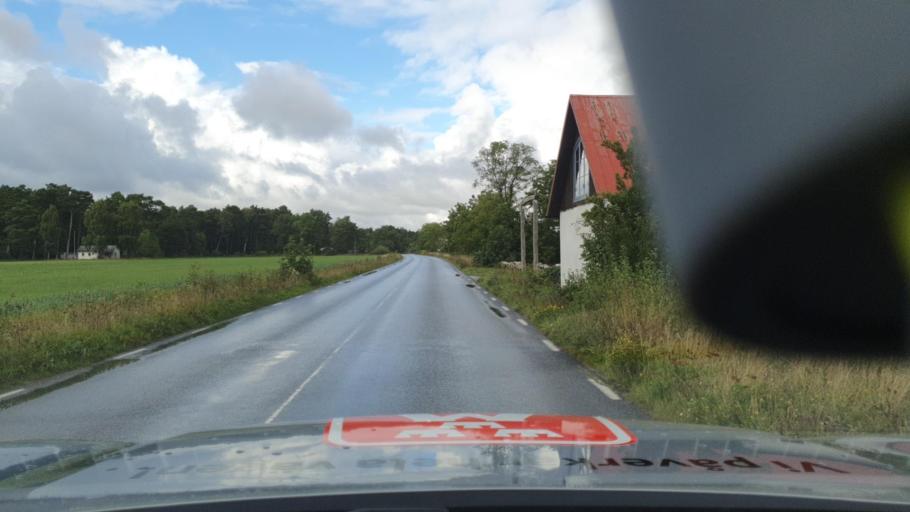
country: SE
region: Gotland
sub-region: Gotland
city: Hemse
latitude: 56.9792
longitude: 18.2406
